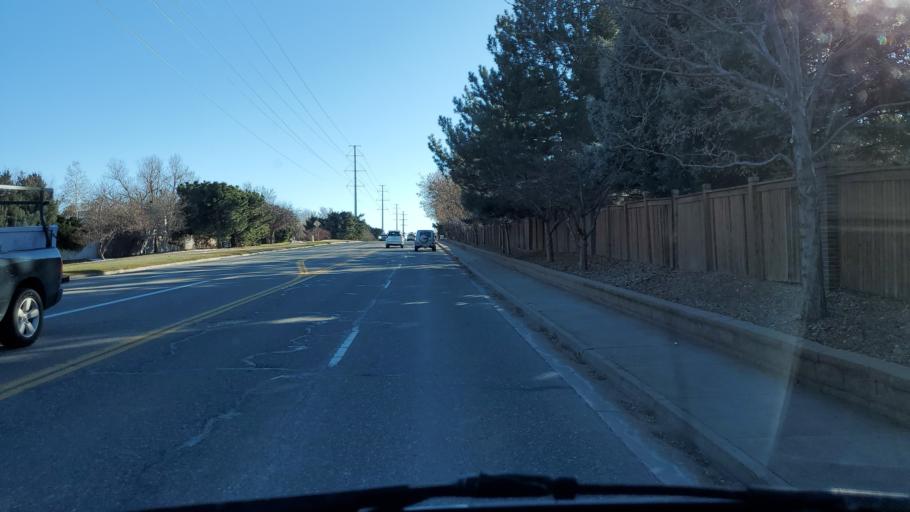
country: US
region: Colorado
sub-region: Arapahoe County
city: Castlewood
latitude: 39.5731
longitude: -104.9044
